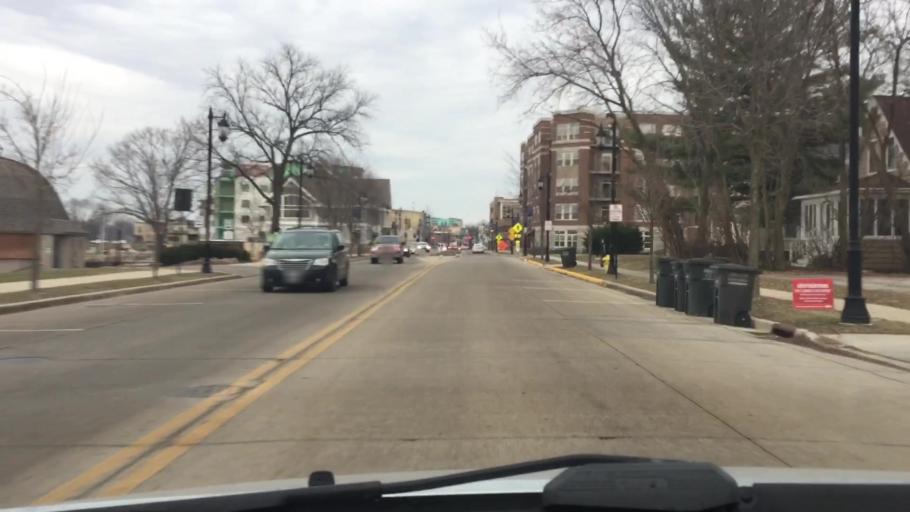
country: US
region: Wisconsin
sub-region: Waukesha County
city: Oconomowoc
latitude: 43.1123
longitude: -88.5039
